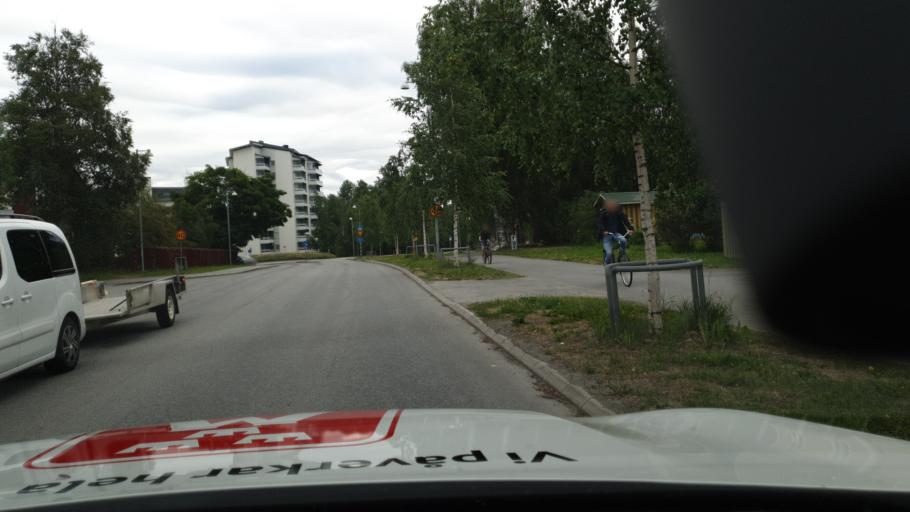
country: SE
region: Vaesterbotten
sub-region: Umea Kommun
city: Umea
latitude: 63.8323
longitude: 20.2244
